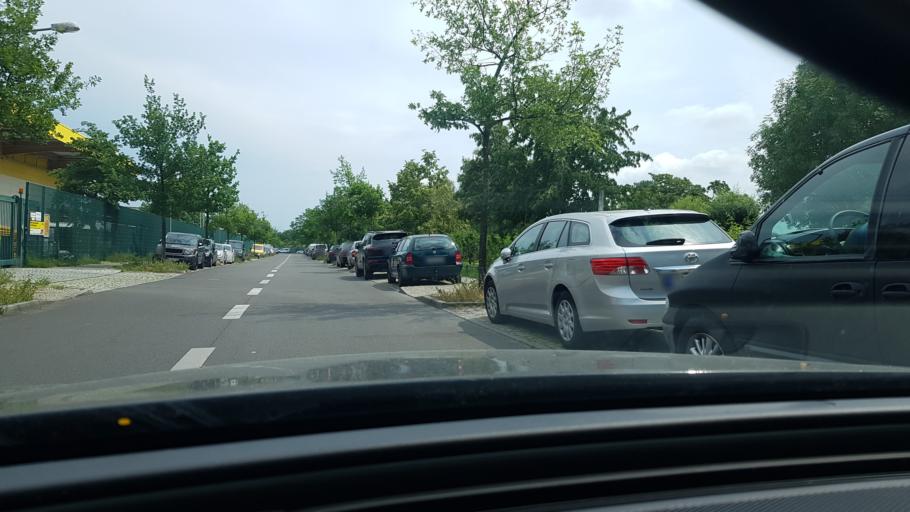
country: DE
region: Berlin
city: Charlottenburg-Nord
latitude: 52.5438
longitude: 13.3095
